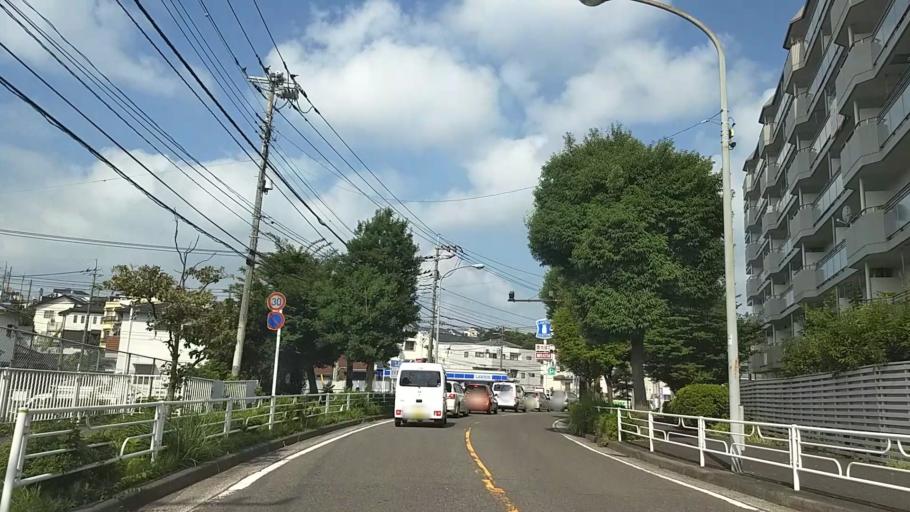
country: JP
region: Kanagawa
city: Yokohama
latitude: 35.4144
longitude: 139.5779
